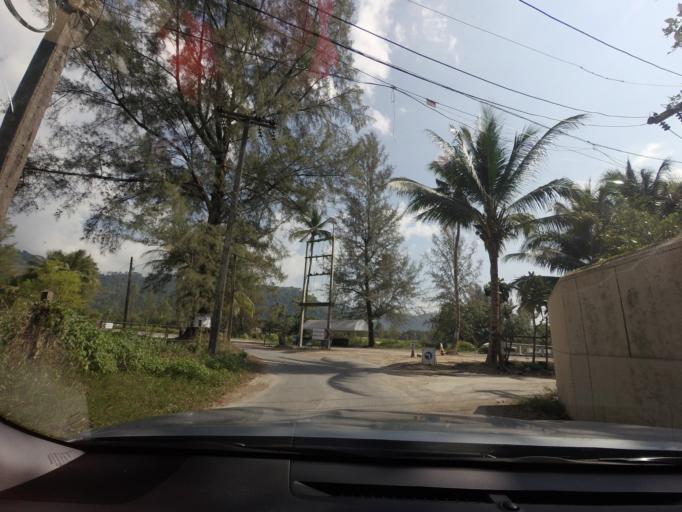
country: TH
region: Phangnga
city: Ban Khao Lak
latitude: 8.6614
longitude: 98.2483
